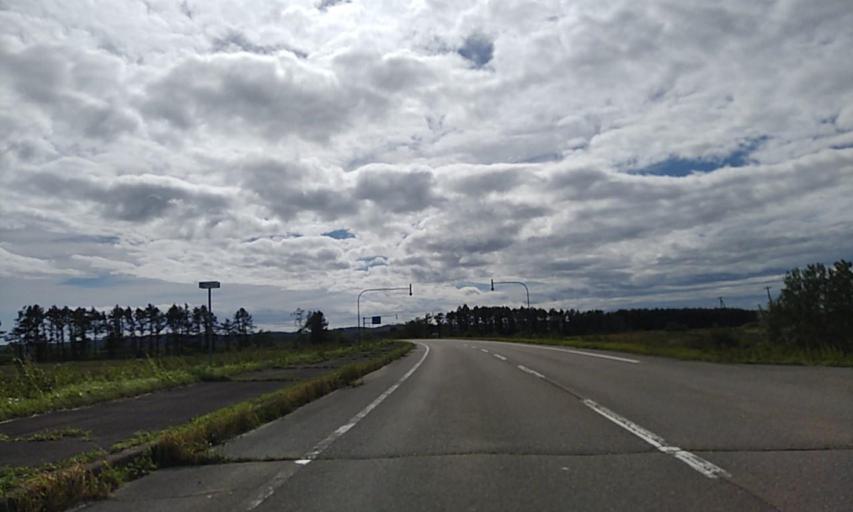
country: JP
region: Hokkaido
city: Obihiro
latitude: 42.7169
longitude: 143.6421
